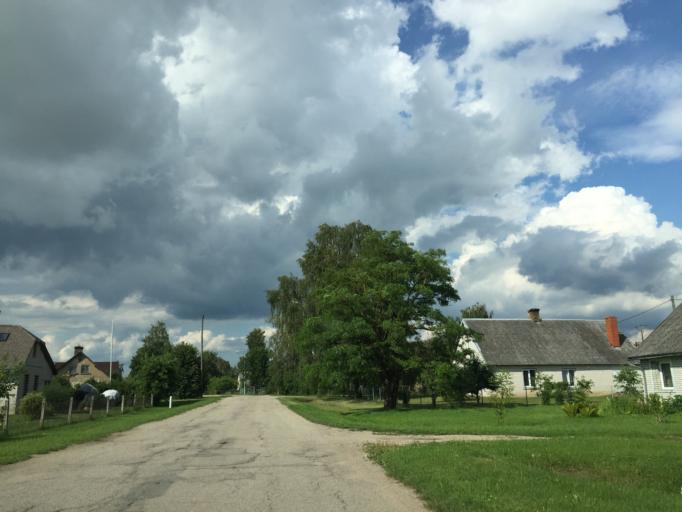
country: LV
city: Tervete
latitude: 56.6115
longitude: 23.4531
